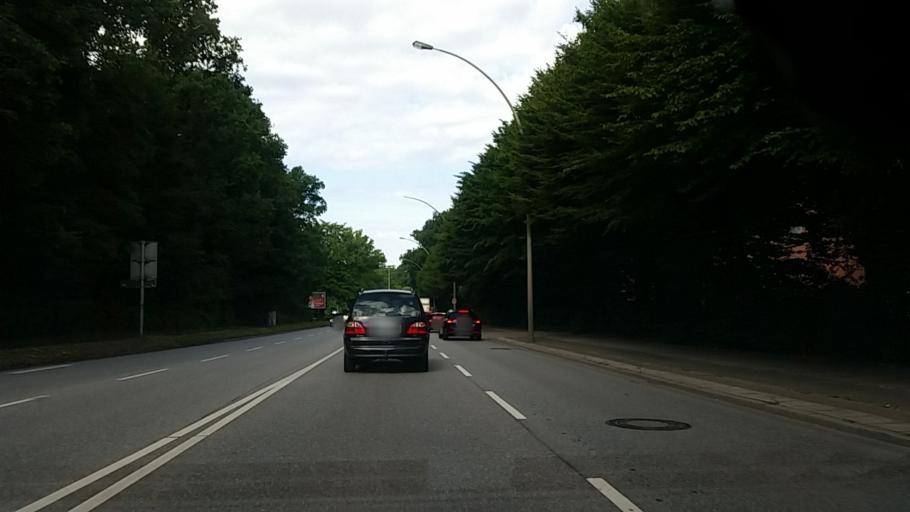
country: DE
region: Hamburg
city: Poppenbuettel
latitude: 53.6563
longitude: 10.0918
